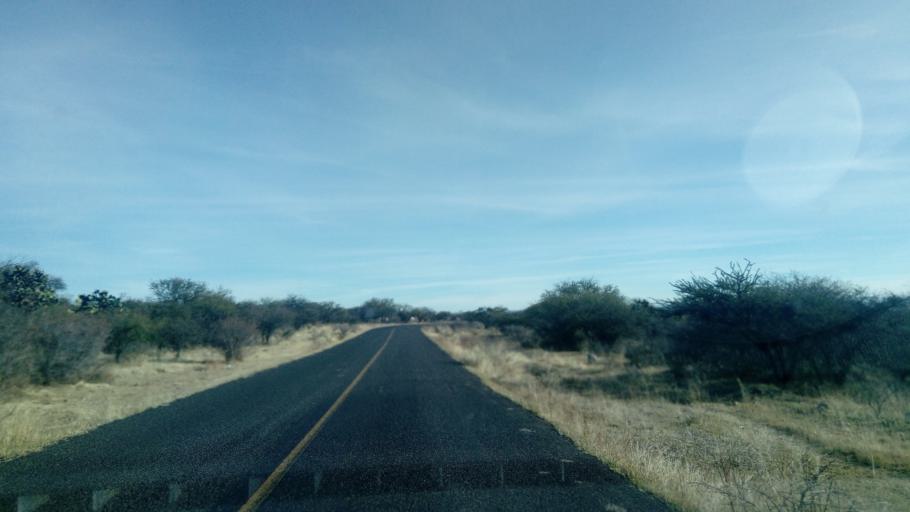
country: MX
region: Durango
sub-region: Nombre de Dios
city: Nombre de Dios
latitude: 23.9404
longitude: -104.3235
